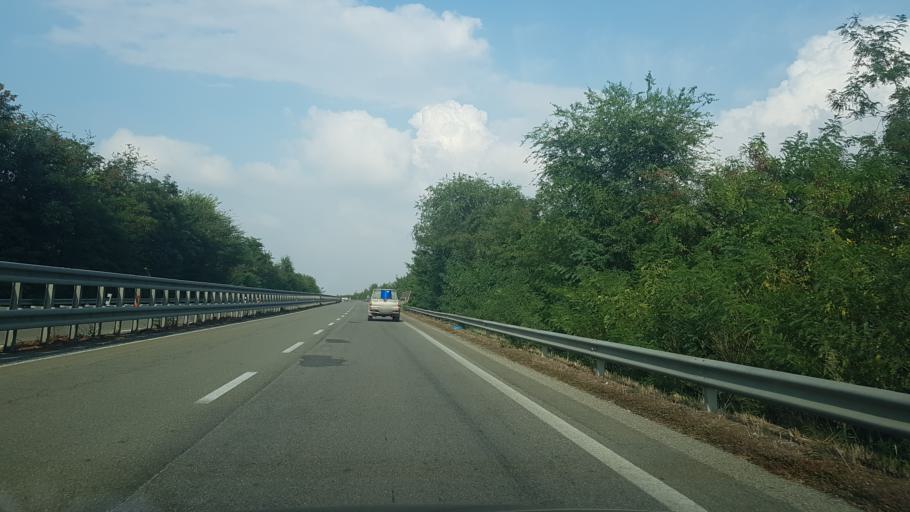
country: IT
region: Piedmont
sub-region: Provincia di Alessandria
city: Alessandria
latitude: 44.8892
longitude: 8.6205
